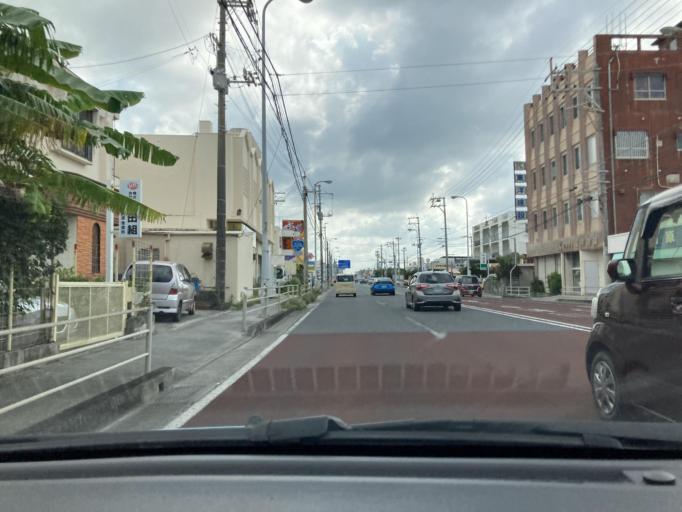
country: JP
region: Okinawa
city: Ginowan
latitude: 26.2140
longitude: 127.7616
